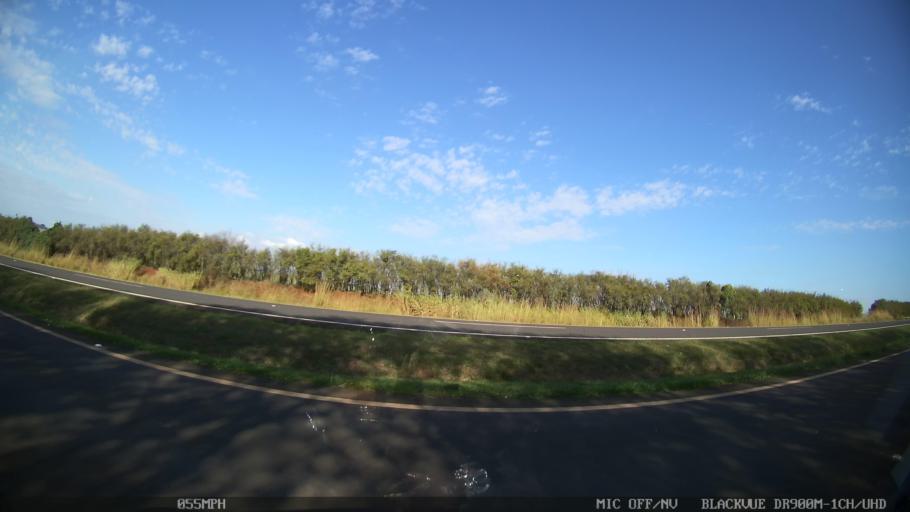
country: BR
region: Sao Paulo
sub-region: Iracemapolis
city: Iracemapolis
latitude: -22.6666
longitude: -47.5361
